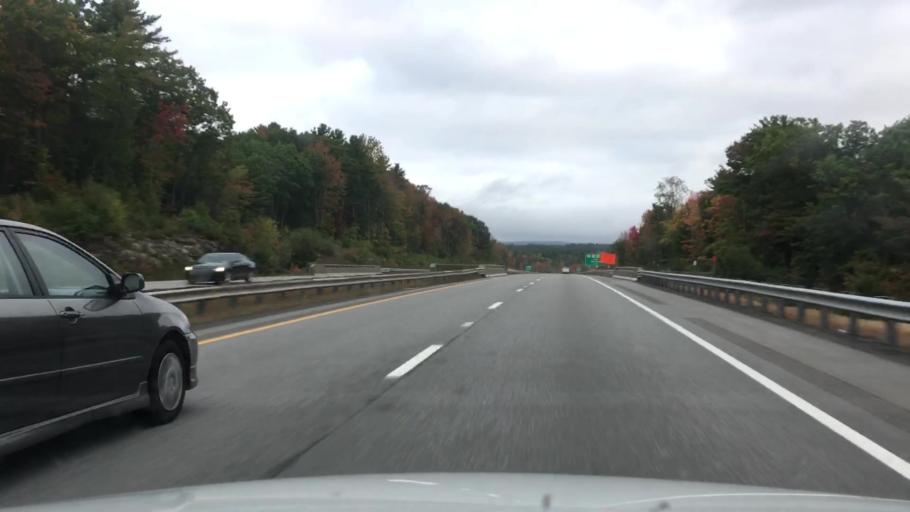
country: US
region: Maine
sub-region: Cumberland County
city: Cumberland Center
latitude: 43.8610
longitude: -70.3243
